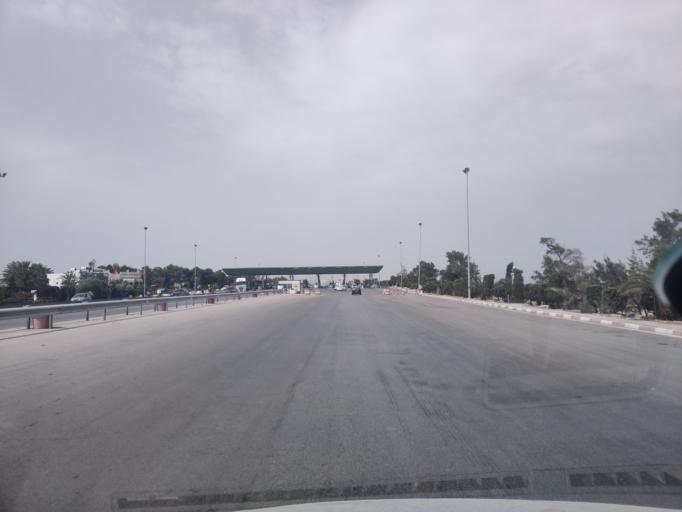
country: TN
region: Susah
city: Sidi Bou Ali
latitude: 36.0022
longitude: 10.4366
